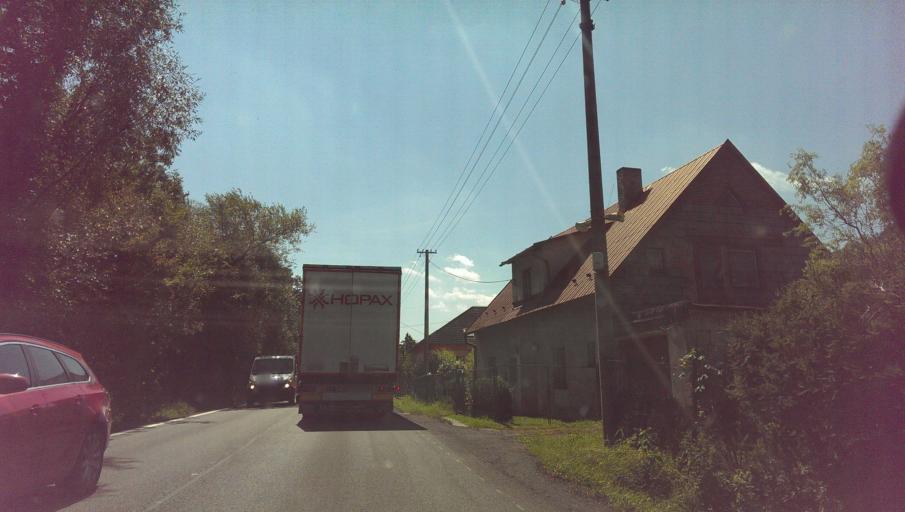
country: CZ
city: Lichnov (o. Novy Jicin)
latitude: 49.5886
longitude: 18.1907
